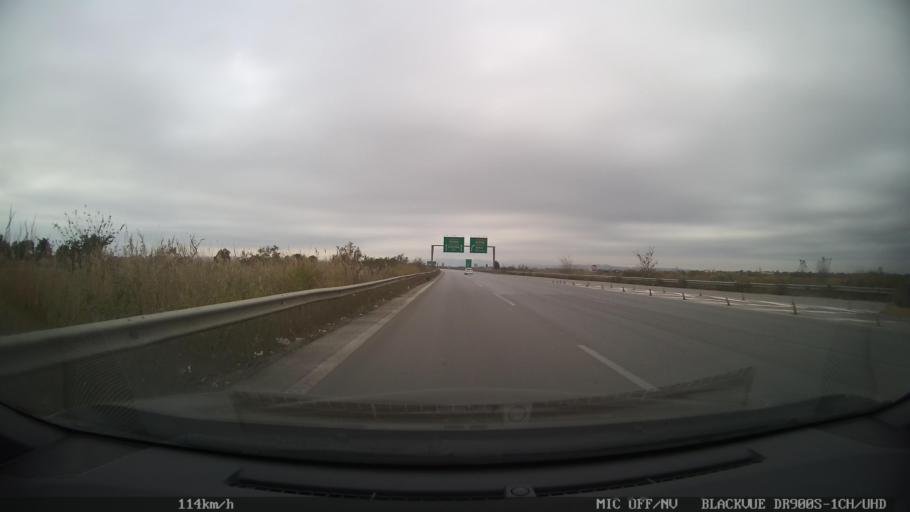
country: GR
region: Central Macedonia
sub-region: Nomos Imathias
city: Kleidi
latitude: 40.5657
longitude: 22.6104
